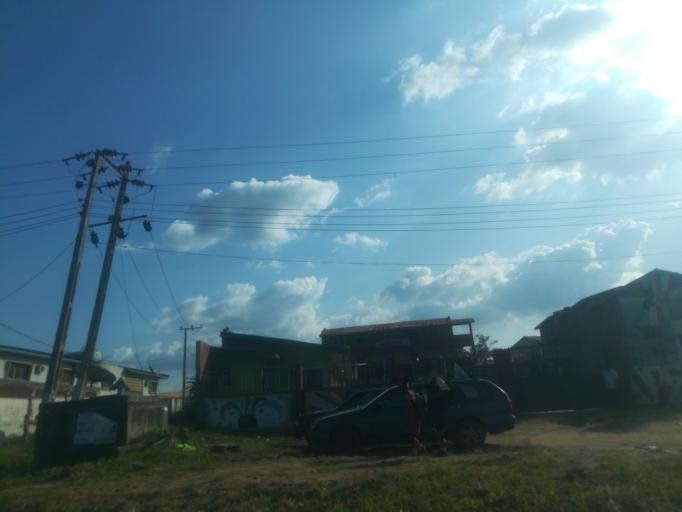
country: NG
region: Oyo
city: Egbeda
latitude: 7.3862
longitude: 3.9818
